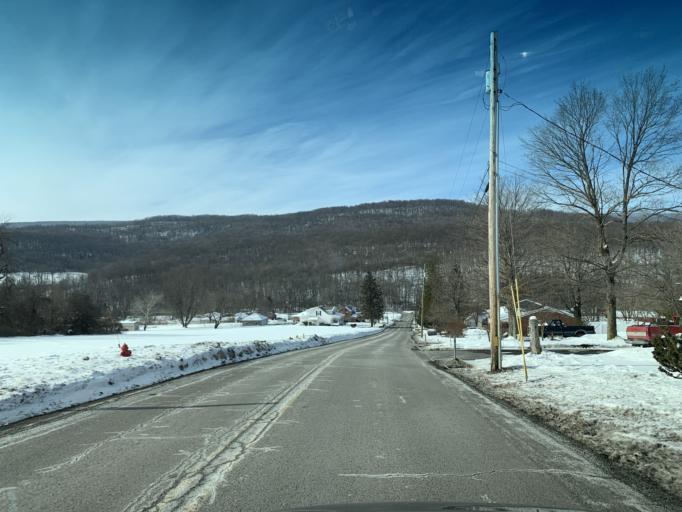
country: US
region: Maryland
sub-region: Allegany County
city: Frostburg
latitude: 39.6748
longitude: -78.8932
